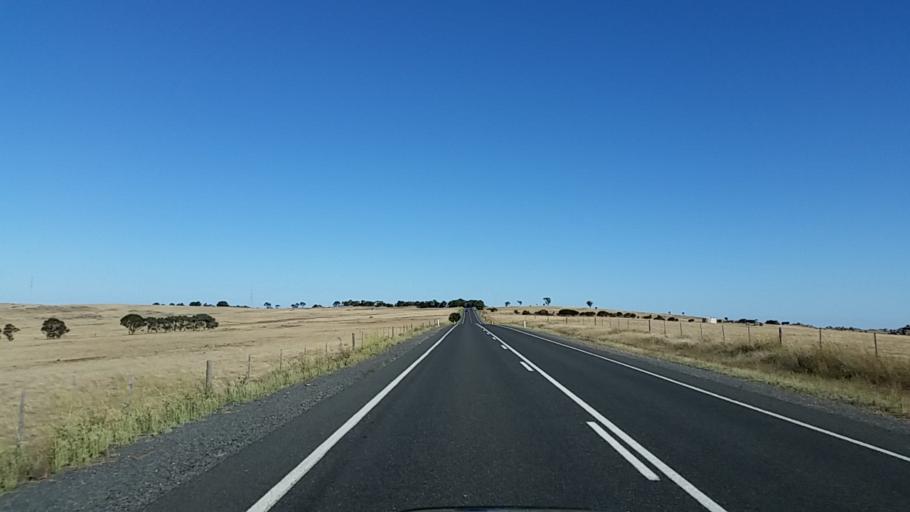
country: AU
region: South Australia
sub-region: Adelaide Hills
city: Birdwood
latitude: -34.7715
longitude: 139.1149
